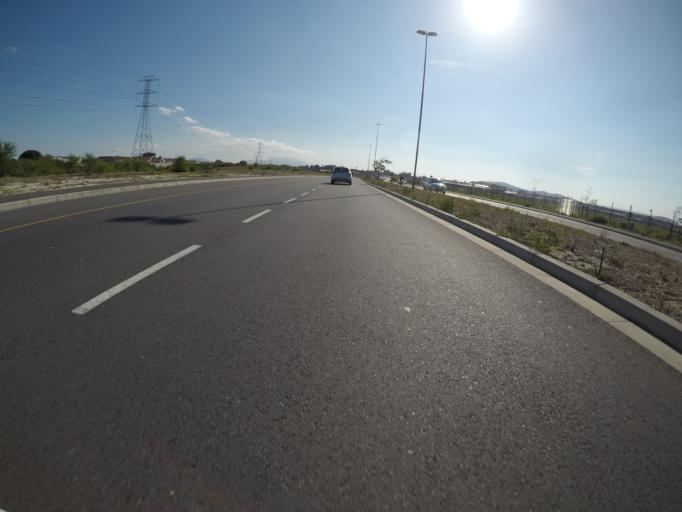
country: ZA
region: Western Cape
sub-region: City of Cape Town
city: Kraaifontein
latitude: -33.9081
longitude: 18.6785
